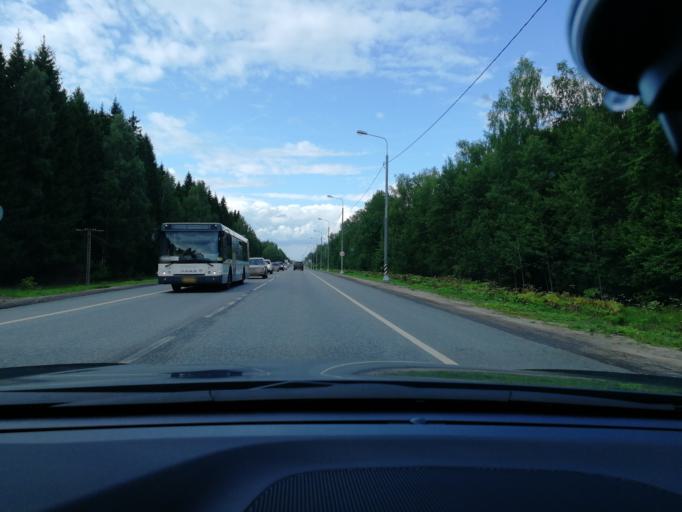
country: RU
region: Moskovskaya
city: Proletarskiy
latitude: 55.0545
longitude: 37.4337
